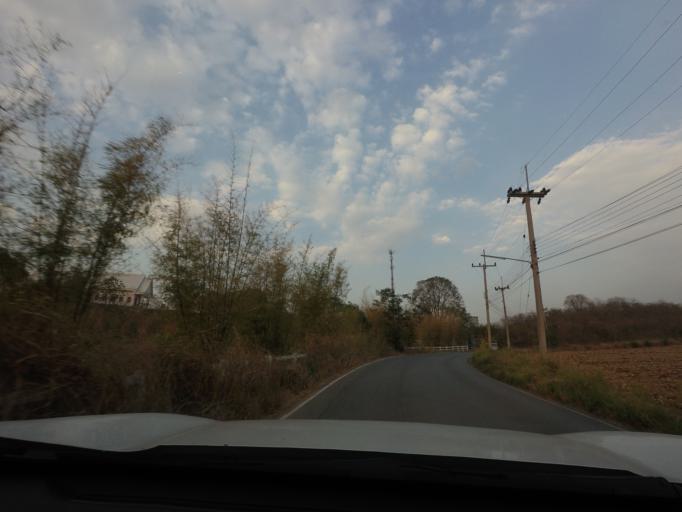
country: TH
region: Nakhon Ratchasima
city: Pak Chong
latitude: 14.6474
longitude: 101.4655
